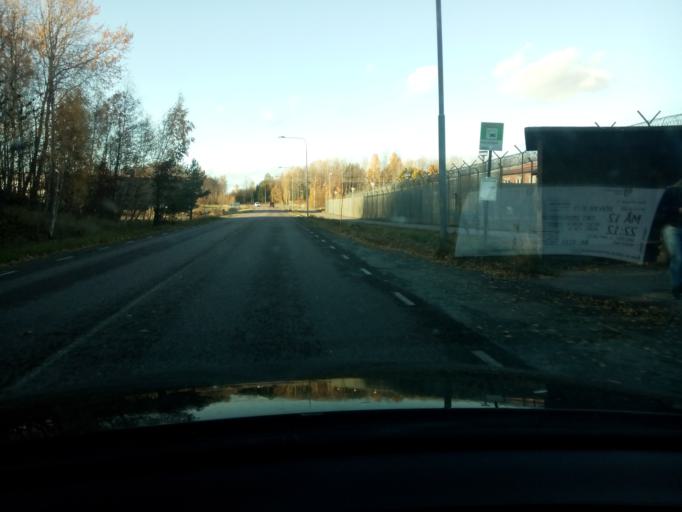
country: SE
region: Soedermanland
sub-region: Nykopings Kommun
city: Nykoping
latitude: 58.7223
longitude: 17.0222
